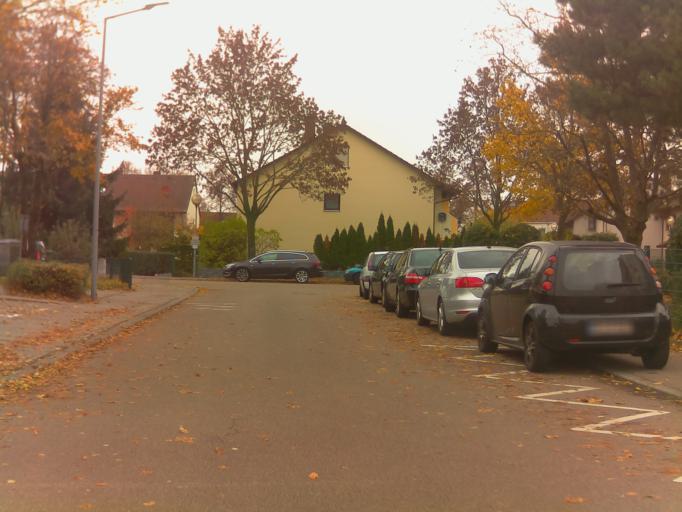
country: DE
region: Baden-Wuerttemberg
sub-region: Karlsruhe Region
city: Weinheim
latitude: 49.5468
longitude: 8.6342
